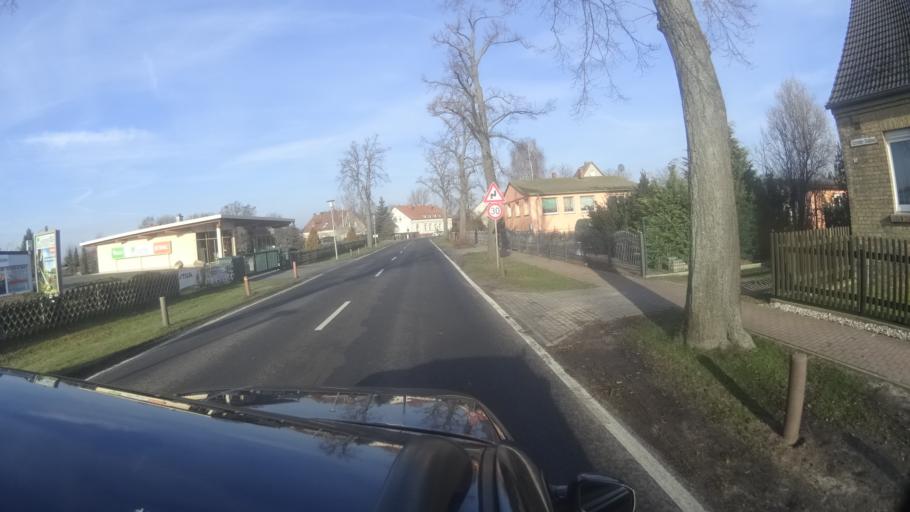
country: DE
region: Brandenburg
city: Velten
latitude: 52.7134
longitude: 13.1017
